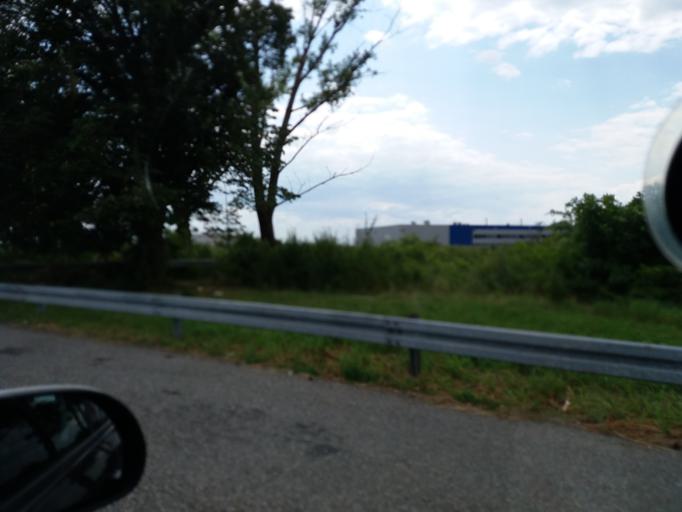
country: RS
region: Autonomna Pokrajina Vojvodina
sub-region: Sremski Okrug
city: Ruma
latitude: 44.9585
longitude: 19.8210
